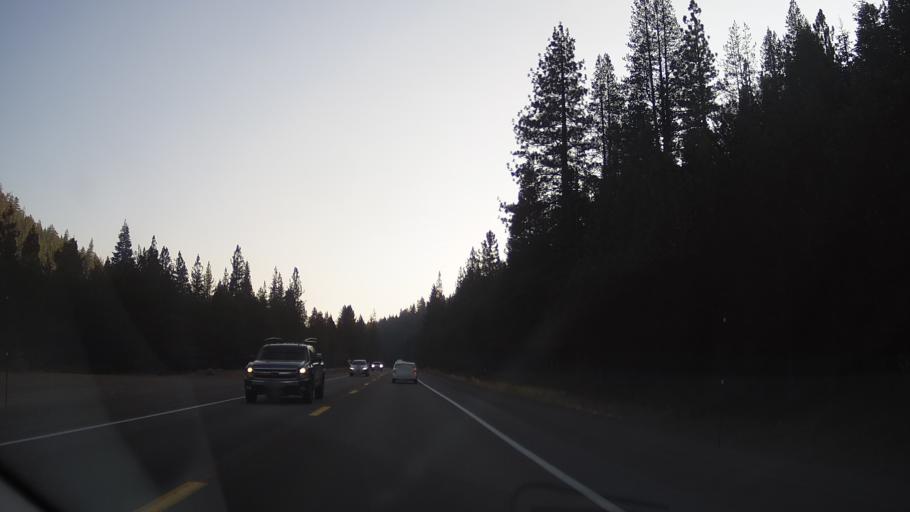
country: US
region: California
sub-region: Nevada County
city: Truckee
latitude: 39.2517
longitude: -120.2114
